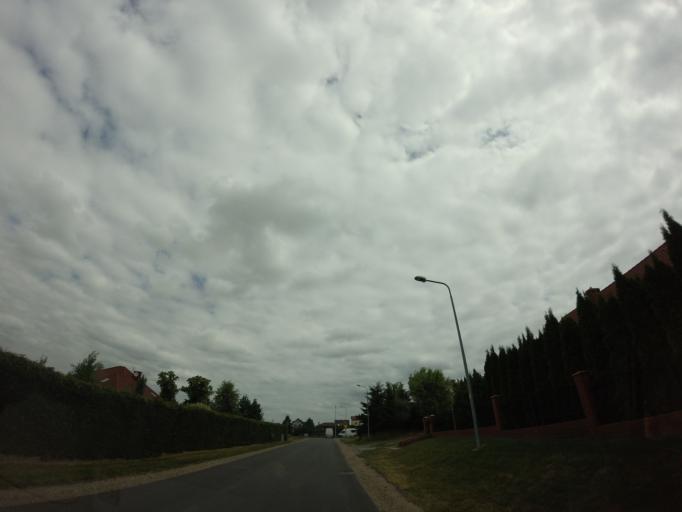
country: PL
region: Lubusz
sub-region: Powiat strzelecko-drezdenecki
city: Strzelce Krajenskie
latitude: 52.8786
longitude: 15.5439
